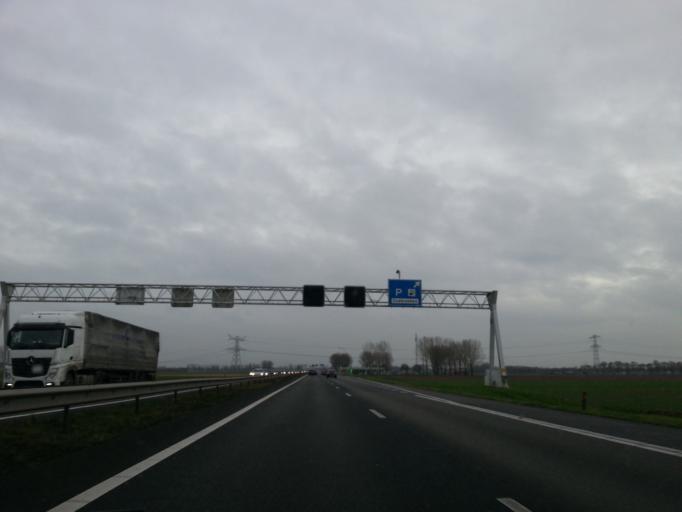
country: NL
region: Gelderland
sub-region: Gemeente Duiven
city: Duiven
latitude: 51.9548
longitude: 6.0448
